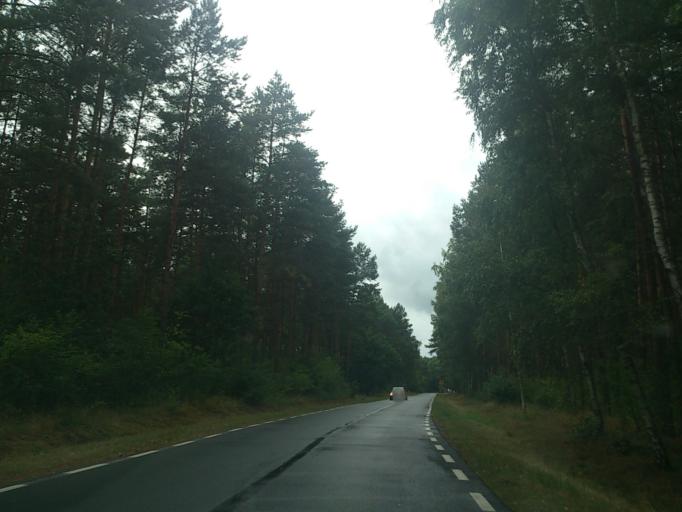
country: PL
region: Greater Poland Voivodeship
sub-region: Powiat gnieznienski
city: Kiszkowo
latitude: 52.5186
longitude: 17.1823
